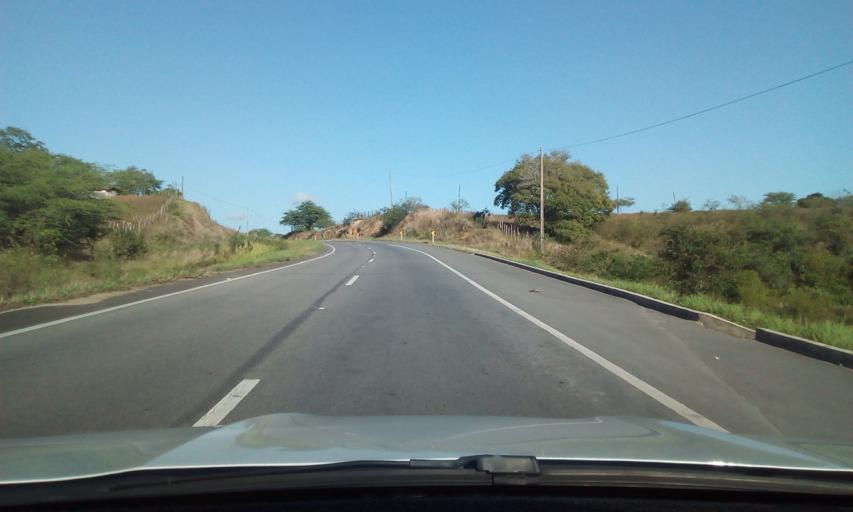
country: BR
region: Paraiba
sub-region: Gurinhem
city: Gurinhem
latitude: -7.1631
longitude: -35.3458
